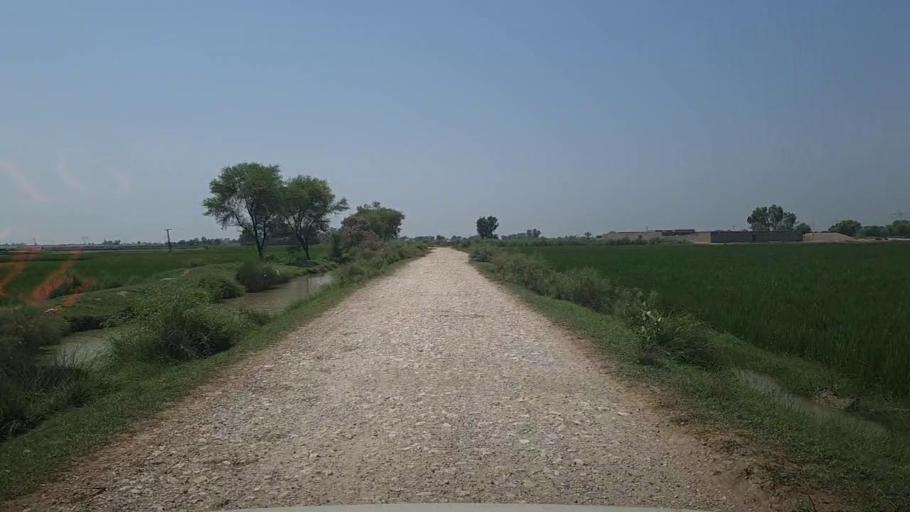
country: PK
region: Sindh
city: Kandhkot
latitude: 28.3221
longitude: 69.3834
